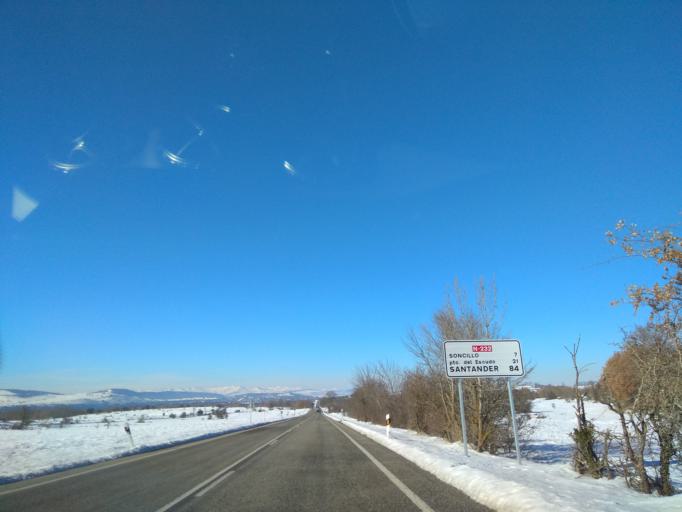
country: ES
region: Cantabria
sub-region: Provincia de Cantabria
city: San Martin de Elines
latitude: 42.9361
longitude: -3.7234
